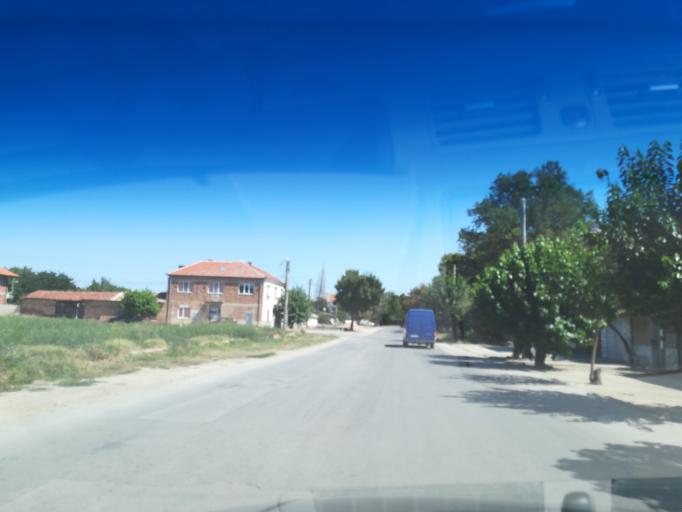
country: BG
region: Pazardzhik
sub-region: Obshtina Pazardzhik
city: Pazardzhik
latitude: 42.2722
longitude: 24.3983
